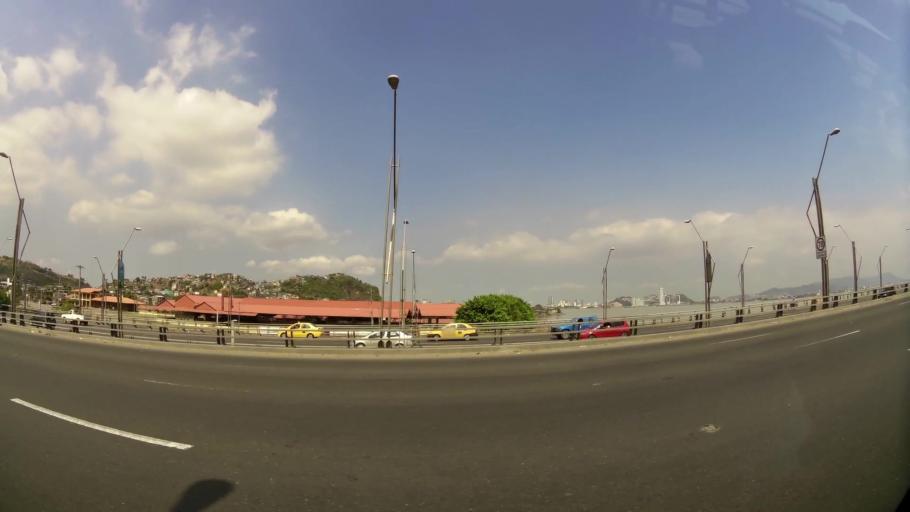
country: EC
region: Guayas
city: Eloy Alfaro
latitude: -2.1634
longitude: -79.8474
